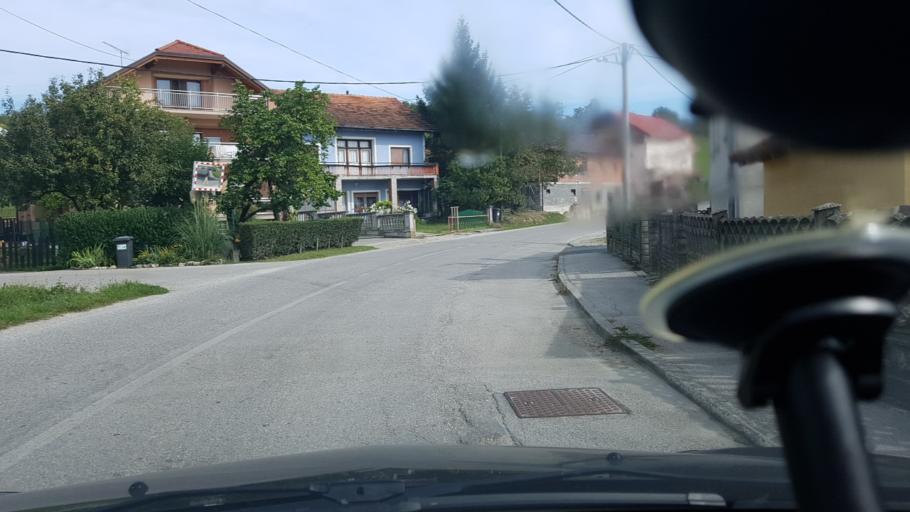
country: HR
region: Varazdinska
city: Remetinec
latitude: 46.0895
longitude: 16.3237
